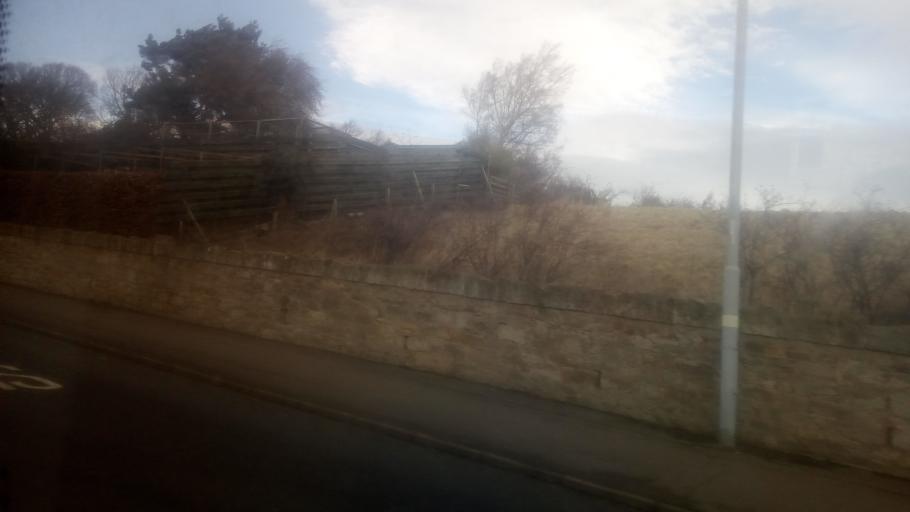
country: GB
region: Scotland
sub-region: Midlothian
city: Dalkeith
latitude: 55.8964
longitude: -3.0797
